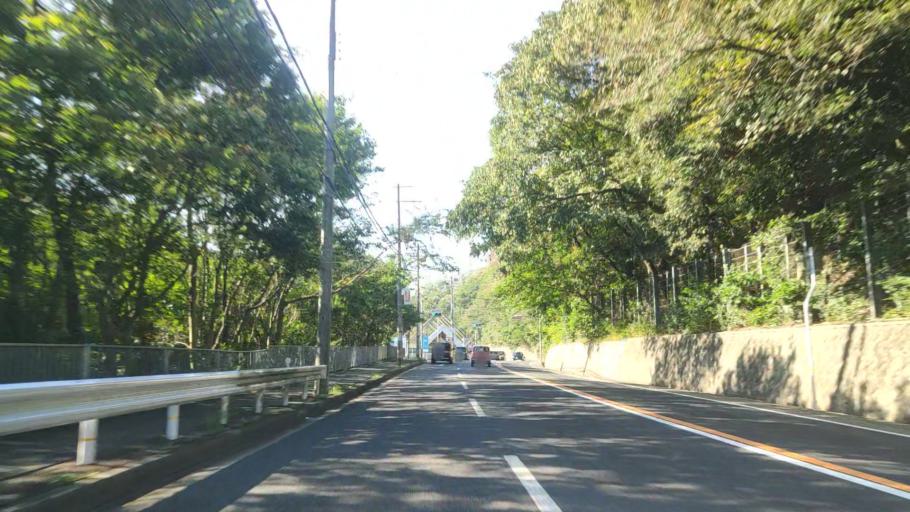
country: JP
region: Hyogo
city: Kobe
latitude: 34.7453
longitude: 135.1597
